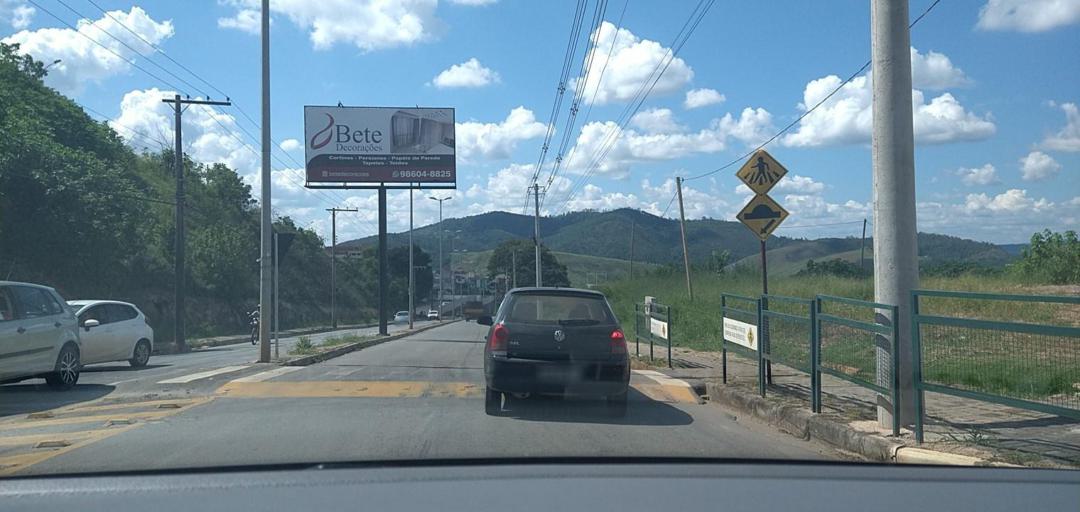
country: BR
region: Minas Gerais
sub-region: Joao Monlevade
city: Joao Monlevade
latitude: -19.8257
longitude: -43.1893
